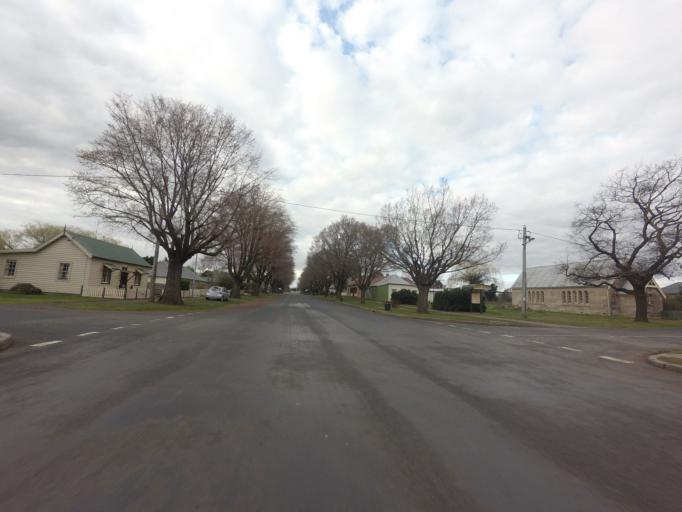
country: AU
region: Tasmania
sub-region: Northern Midlands
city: Evandale
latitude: -42.0290
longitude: 147.4926
